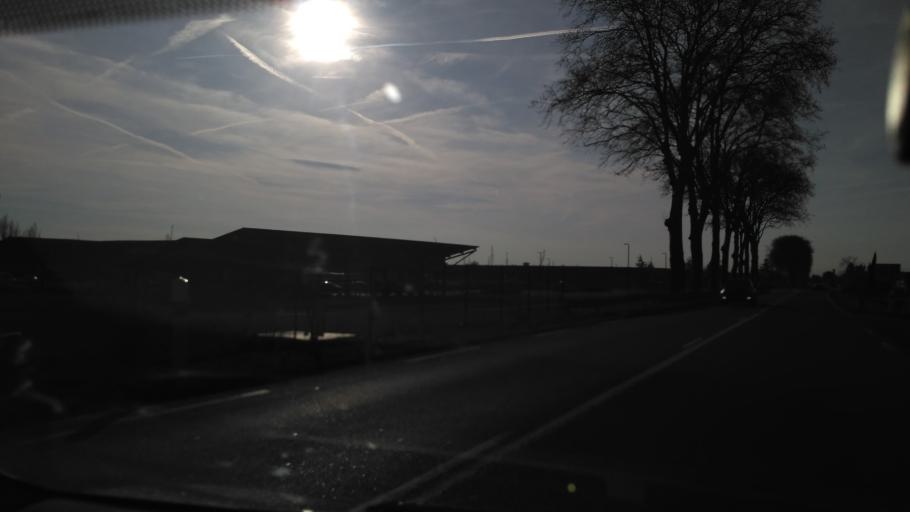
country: FR
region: Rhone-Alpes
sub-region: Departement de la Drome
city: Saint-Paul-les-Romans
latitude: 45.0617
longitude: 5.1092
